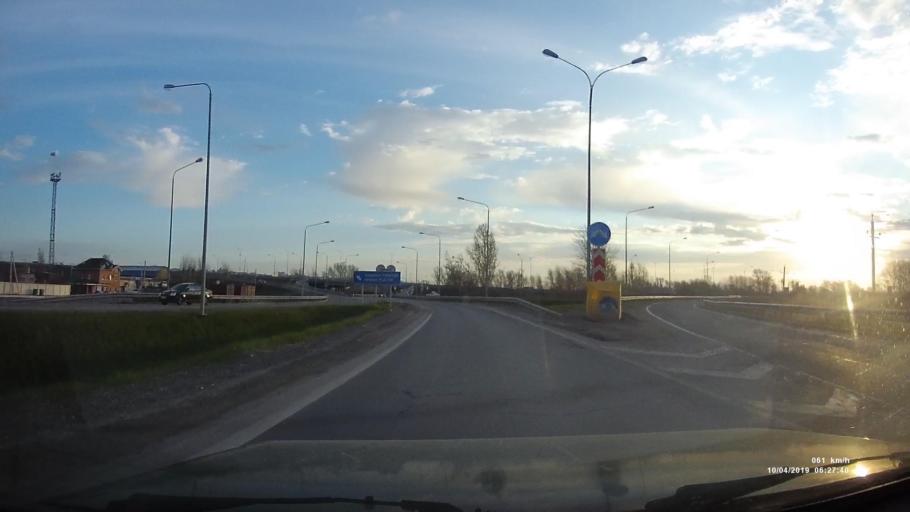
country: RU
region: Rostov
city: Aksay
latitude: 47.2355
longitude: 39.8538
